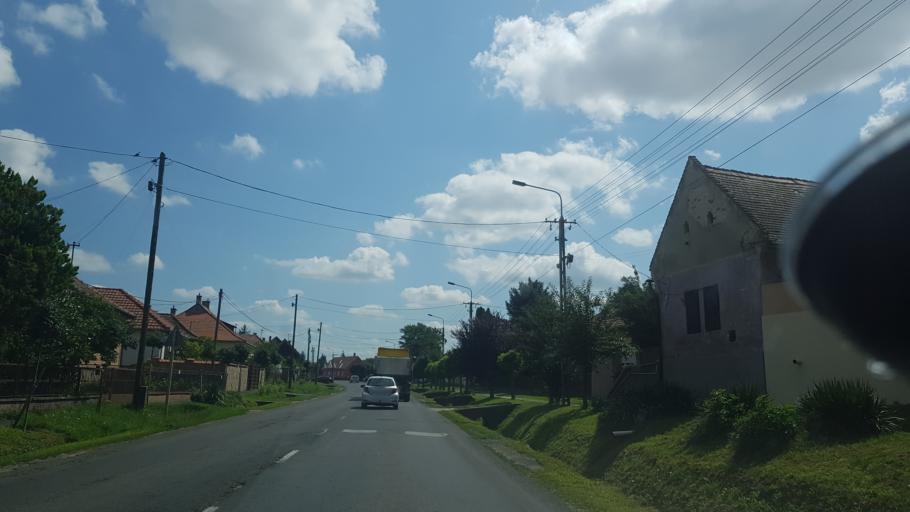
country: HU
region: Somogy
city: Kethely
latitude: 46.6430
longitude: 17.3944
